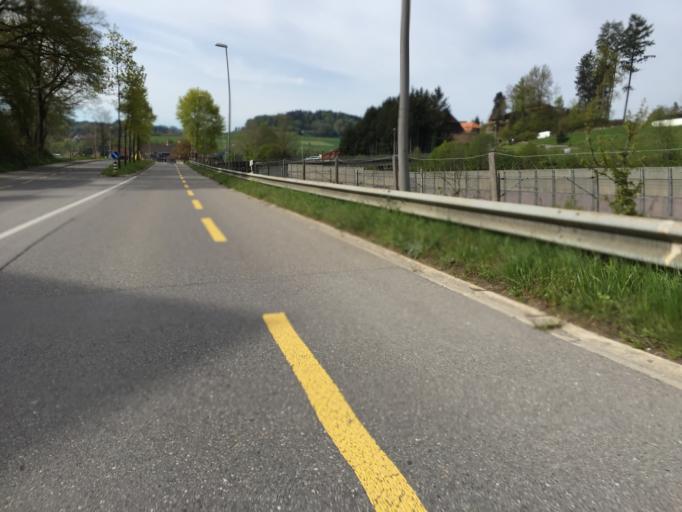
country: CH
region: Fribourg
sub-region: Sense District
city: Flamatt
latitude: 46.8970
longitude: 7.3526
